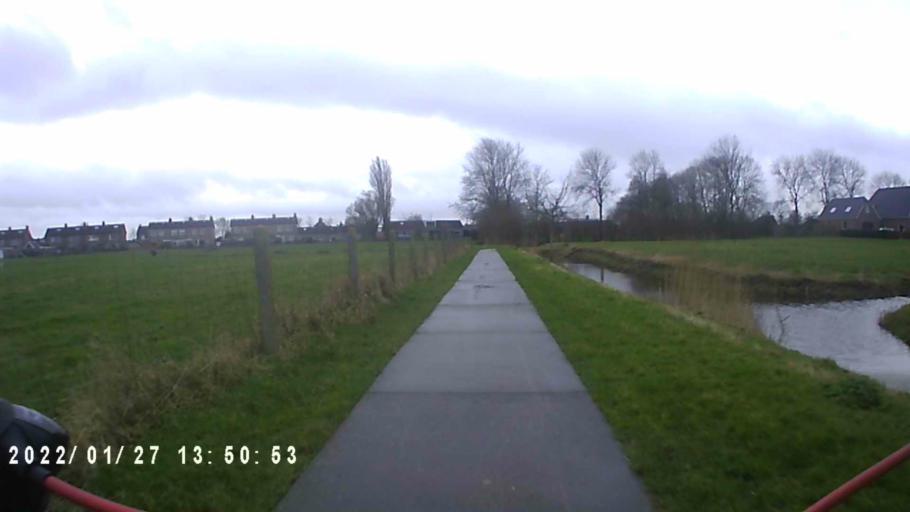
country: NL
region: Friesland
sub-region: Gemeente Kollumerland en Nieuwkruisland
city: Kollum
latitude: 53.3059
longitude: 6.1924
